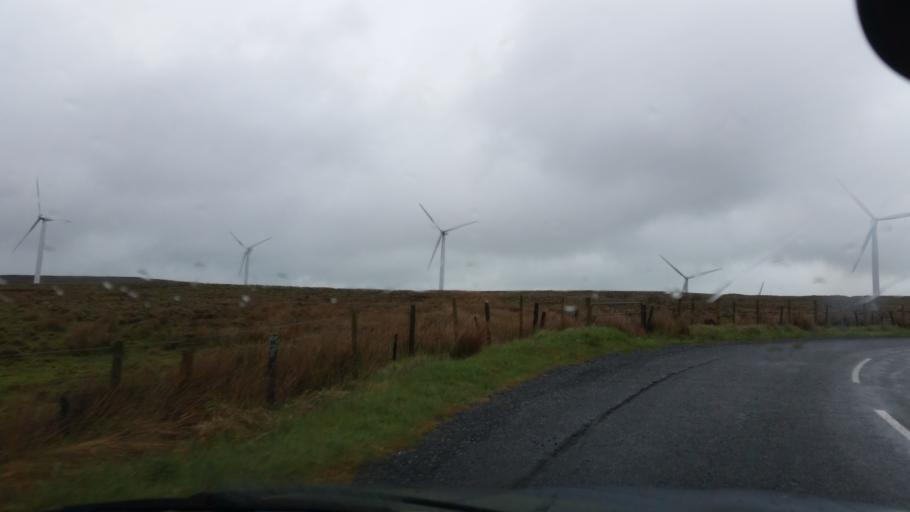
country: GB
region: Northern Ireland
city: Fintona
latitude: 54.4452
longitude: -7.3257
